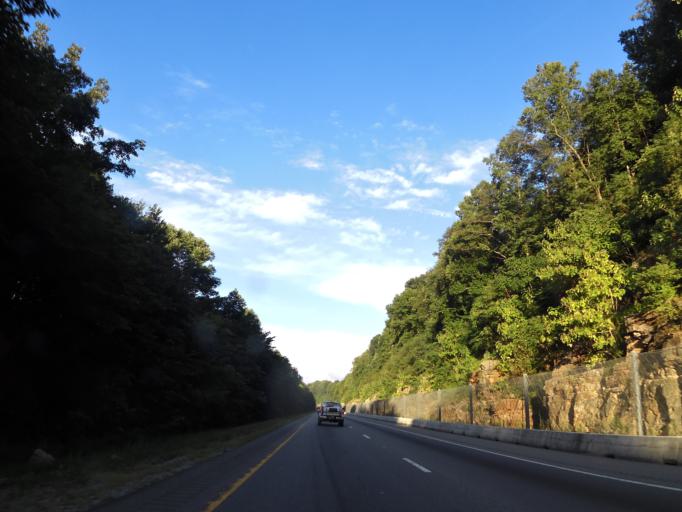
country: US
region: Tennessee
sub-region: Putnam County
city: Algood
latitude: 36.1417
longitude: -85.3888
